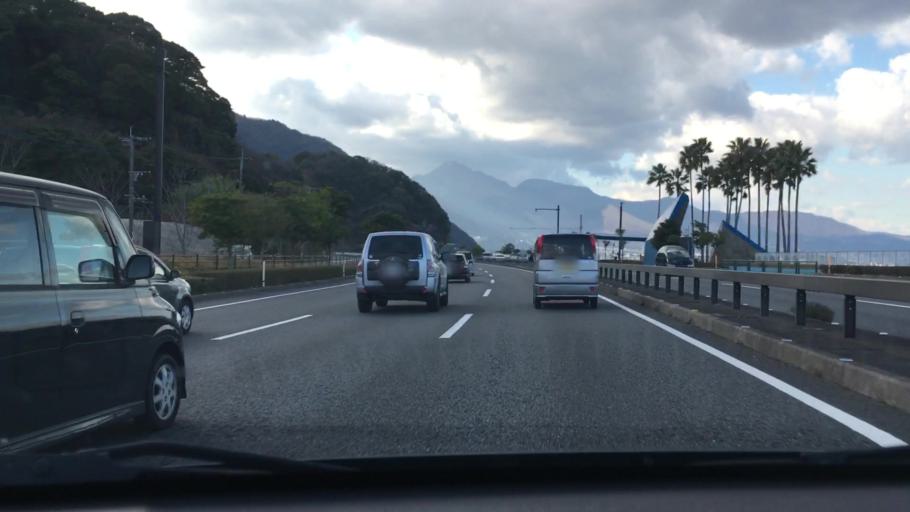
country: JP
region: Oita
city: Oita
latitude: 33.2550
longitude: 131.5609
